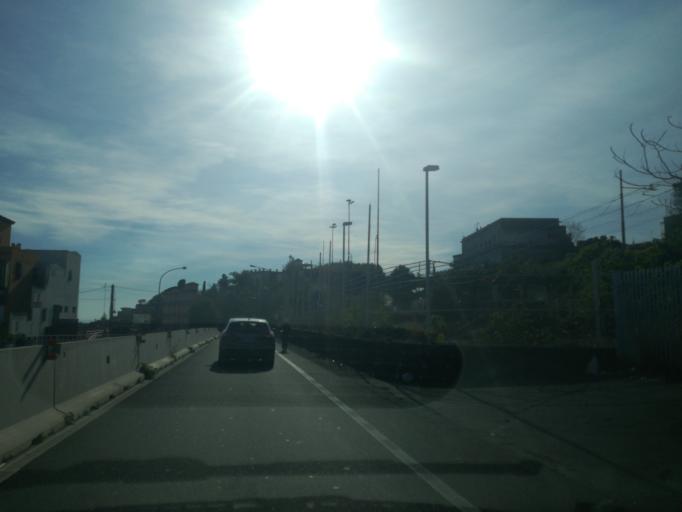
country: IT
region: Sicily
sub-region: Catania
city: Acireale
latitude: 37.6074
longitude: 15.1689
